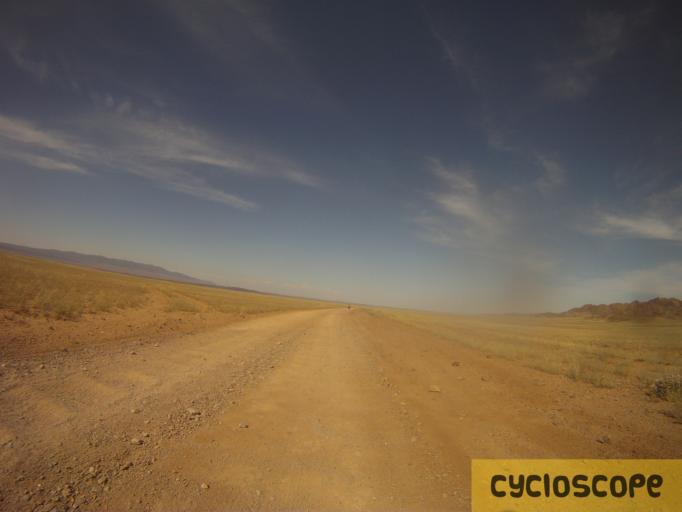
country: KZ
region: Almaty Oblysy
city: Kegen
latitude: 43.3497
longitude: 78.9354
